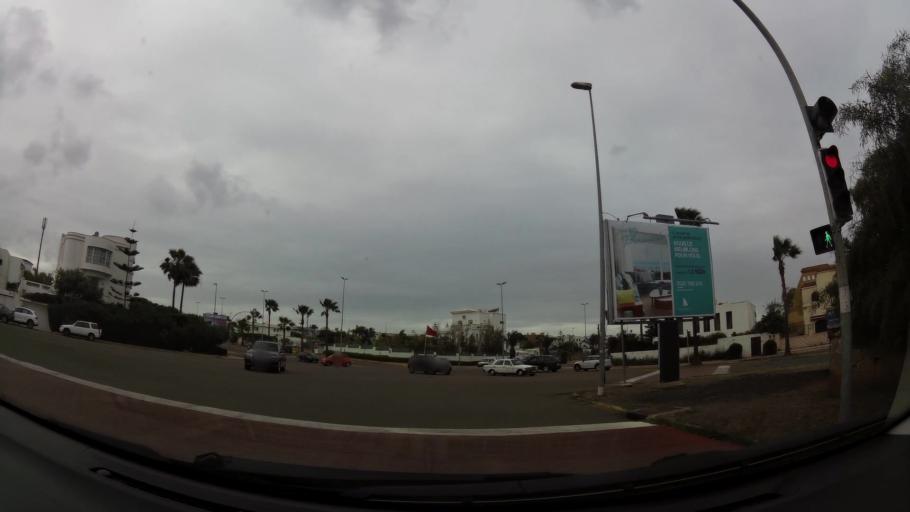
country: MA
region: Grand Casablanca
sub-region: Casablanca
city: Casablanca
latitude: 33.5982
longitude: -7.6547
